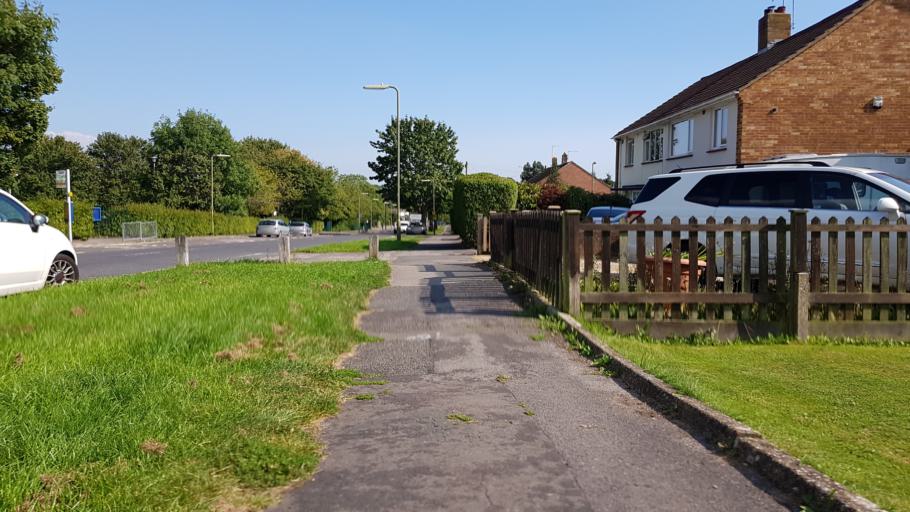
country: GB
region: England
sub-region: Hampshire
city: Waterlooville
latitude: 50.8737
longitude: -1.0351
